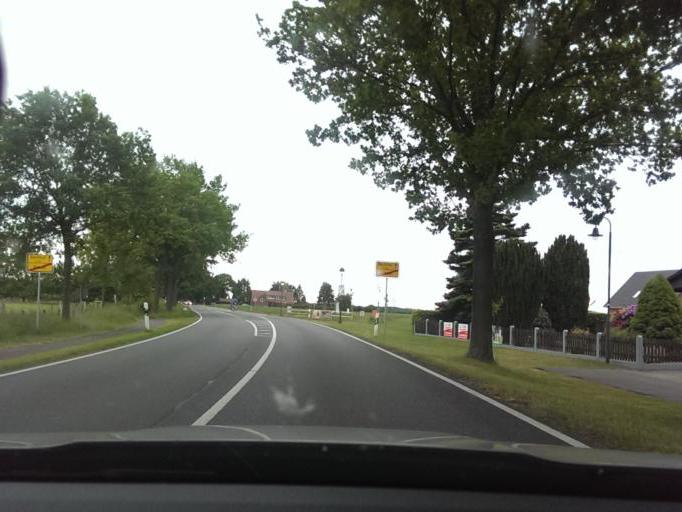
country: DE
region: Lower Saxony
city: Essel
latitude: 52.6887
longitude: 9.6446
